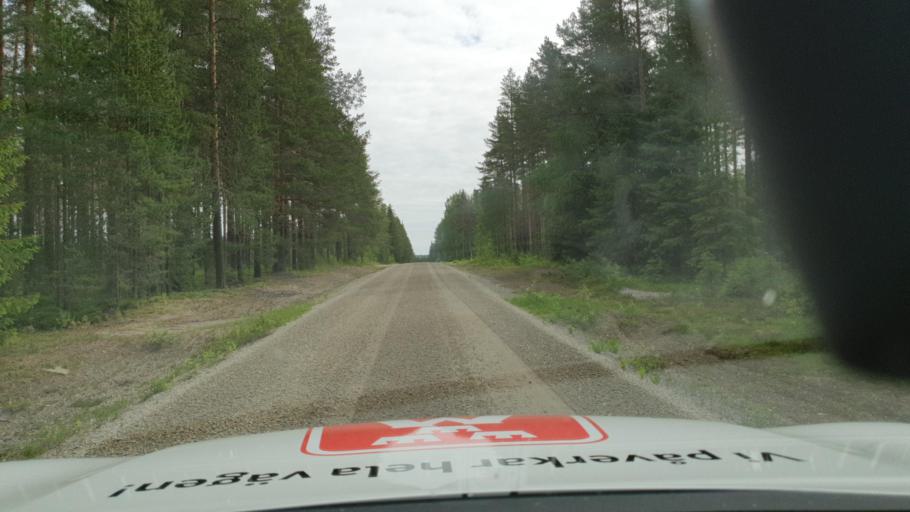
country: SE
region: Vaesterbotten
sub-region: Skelleftea Kommun
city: Forsbacka
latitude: 64.6555
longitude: 20.4228
